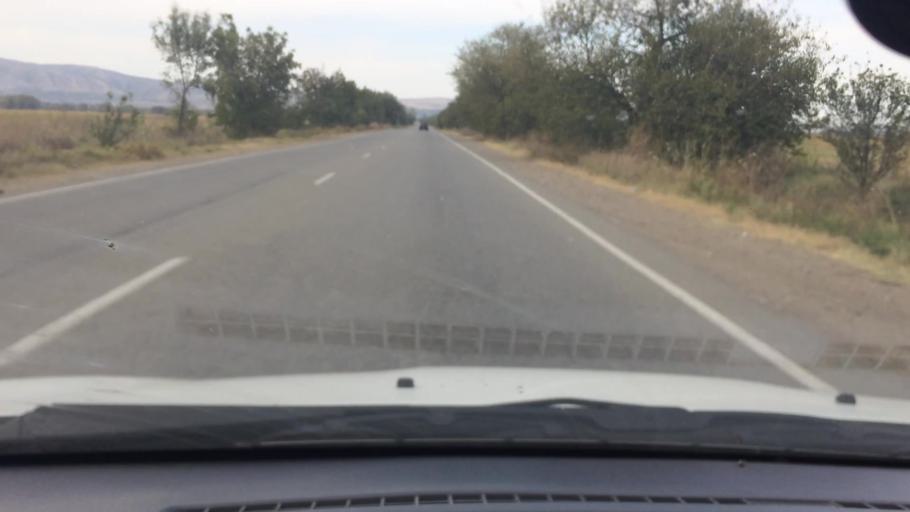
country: GE
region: Kvemo Kartli
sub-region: Marneuli
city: Marneuli
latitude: 41.5587
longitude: 44.7759
